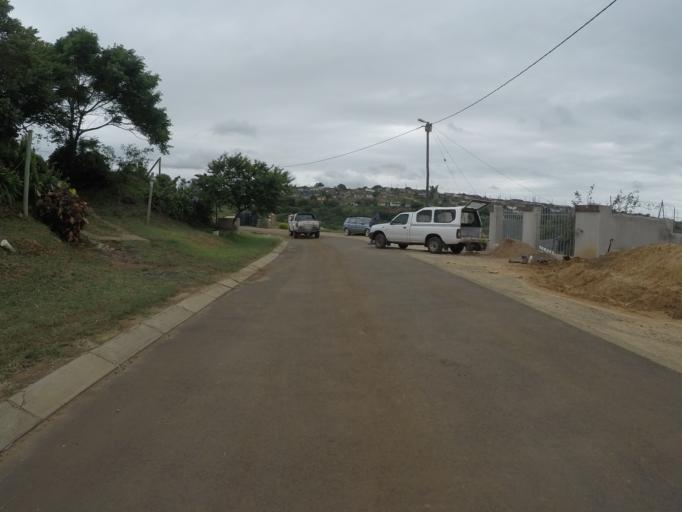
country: ZA
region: KwaZulu-Natal
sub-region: uThungulu District Municipality
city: Empangeni
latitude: -28.7714
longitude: 31.8727
